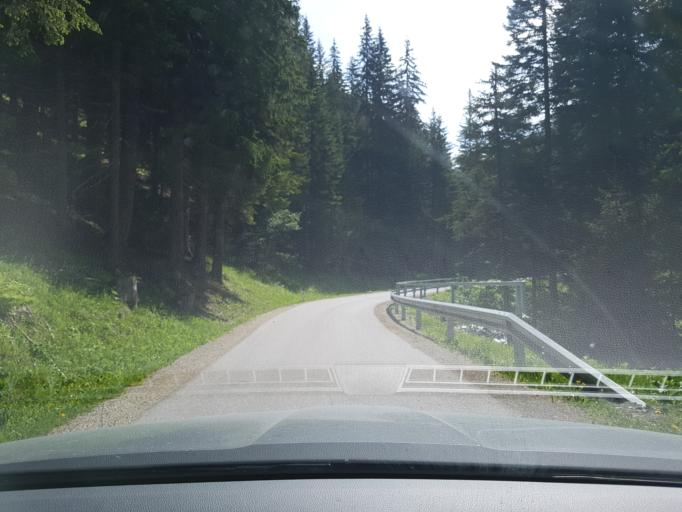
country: AT
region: Salzburg
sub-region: Politischer Bezirk Tamsweg
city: Thomatal
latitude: 47.0344
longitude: 13.7315
